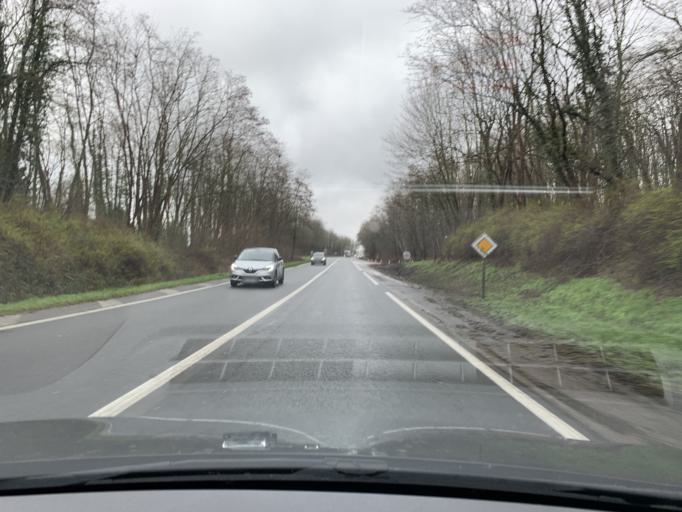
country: FR
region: Nord-Pas-de-Calais
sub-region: Departement du Nord
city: Dechy
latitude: 50.3549
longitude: 3.1222
